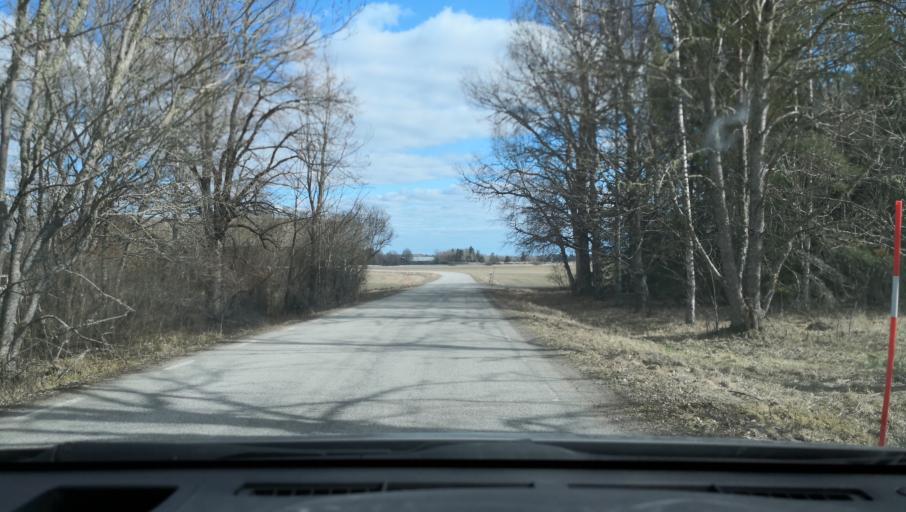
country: SE
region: Vaestmanland
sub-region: Sala Kommun
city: Sala
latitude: 59.8600
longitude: 16.6232
